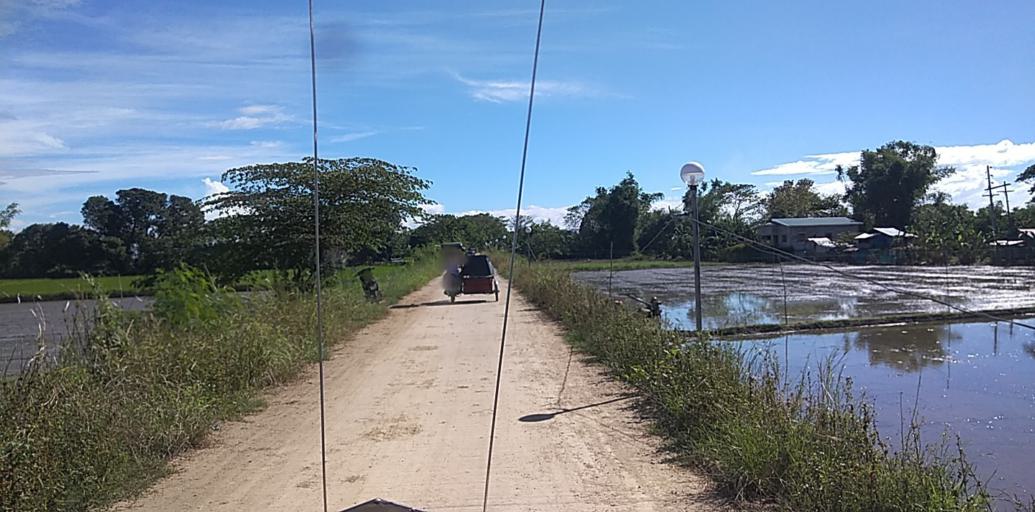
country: PH
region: Central Luzon
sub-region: Province of Pampanga
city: San Nicolas
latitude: 15.0646
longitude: 120.8077
